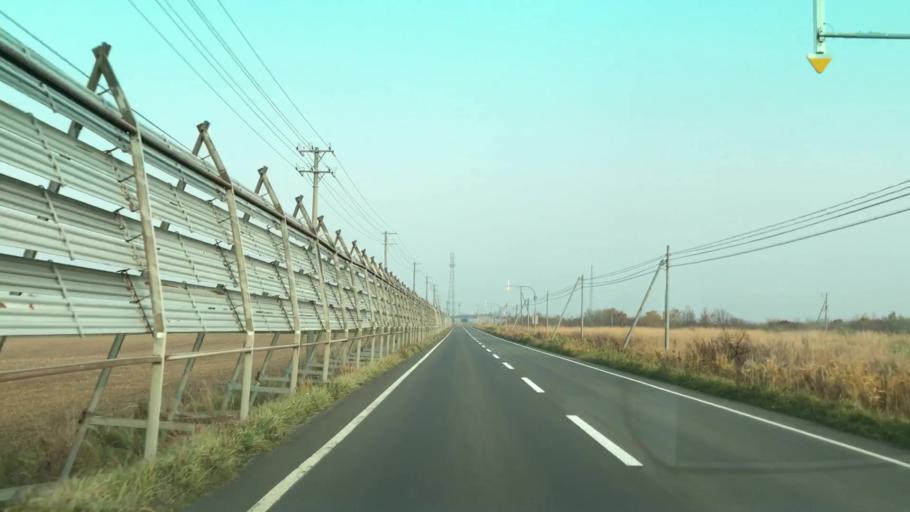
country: JP
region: Hokkaido
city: Ishikari
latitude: 43.2840
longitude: 141.4099
